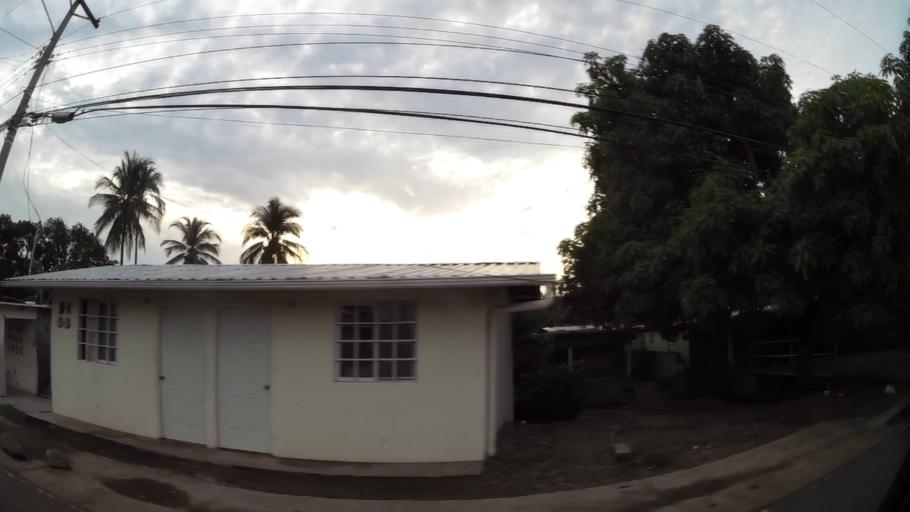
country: PA
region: Panama
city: Tocumen
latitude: 9.0872
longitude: -79.3895
